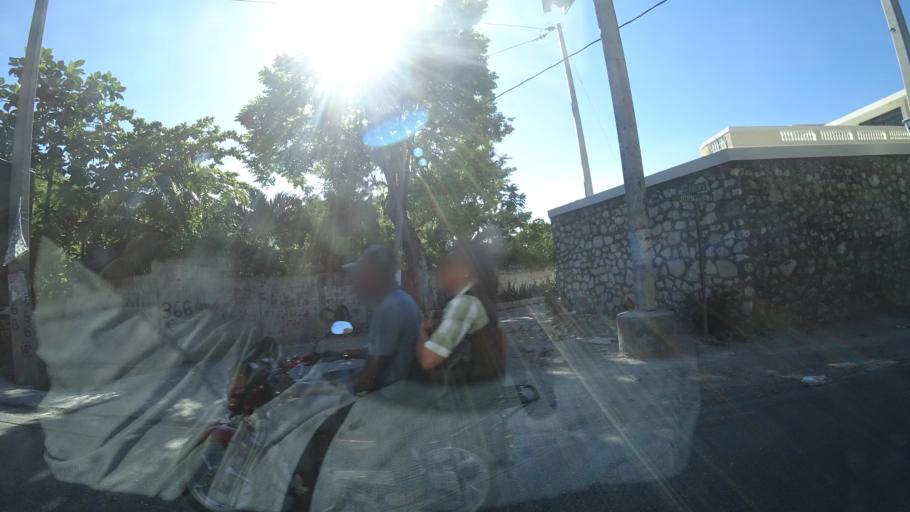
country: HT
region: Ouest
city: Delmas 73
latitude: 18.5354
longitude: -72.3109
